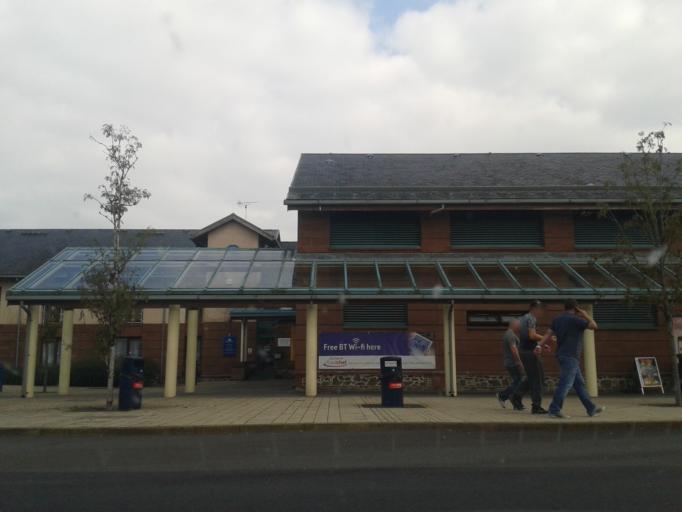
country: GB
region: Scotland
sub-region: Dumfries and Galloway
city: Lochmaben
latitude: 55.2200
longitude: -3.4111
